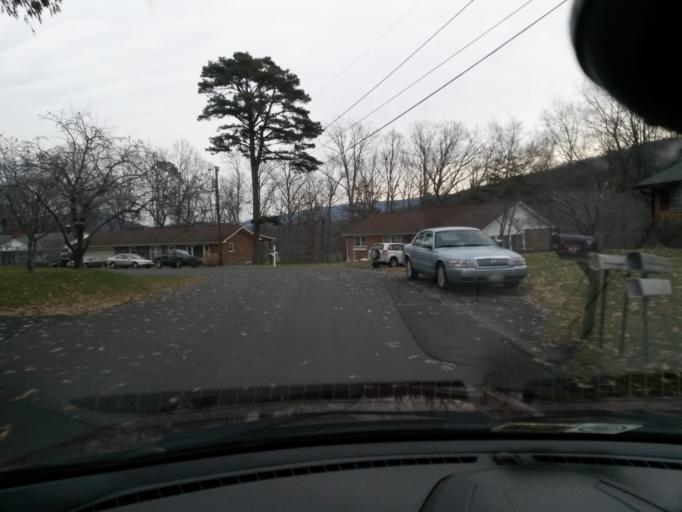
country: US
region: Virginia
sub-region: Alleghany County
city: Clifton Forge
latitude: 37.8189
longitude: -79.8022
